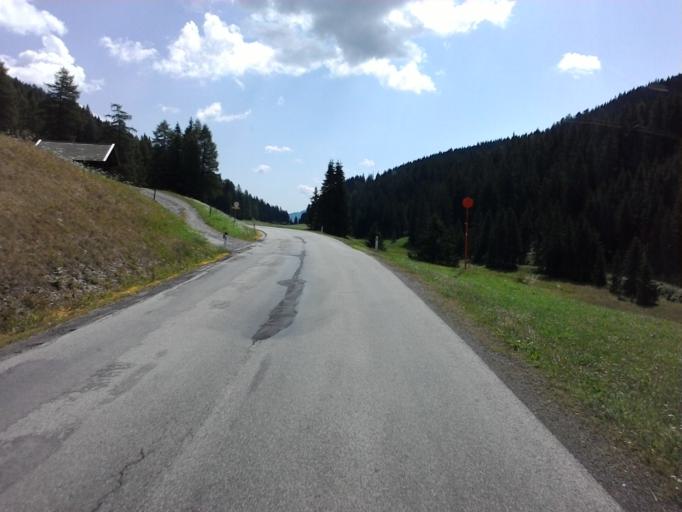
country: AT
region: Tyrol
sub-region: Politischer Bezirk Lienz
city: Kartitsch
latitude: 46.7190
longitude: 12.5309
